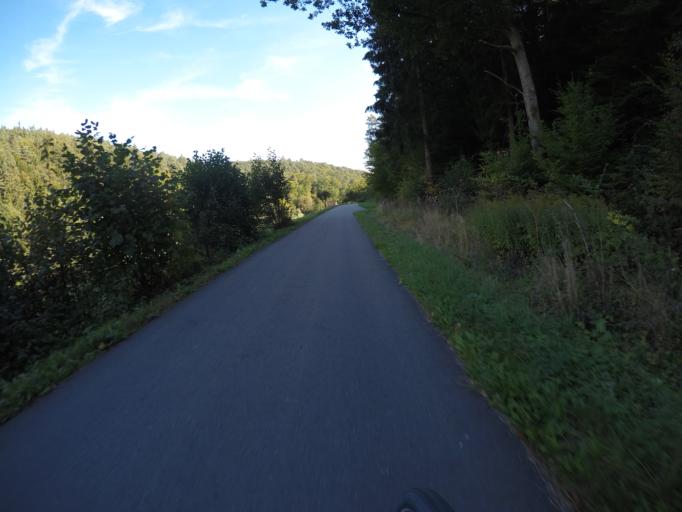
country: DE
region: Baden-Wuerttemberg
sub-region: Regierungsbezirk Stuttgart
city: Waldenbuch
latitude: 48.6446
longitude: 9.1646
